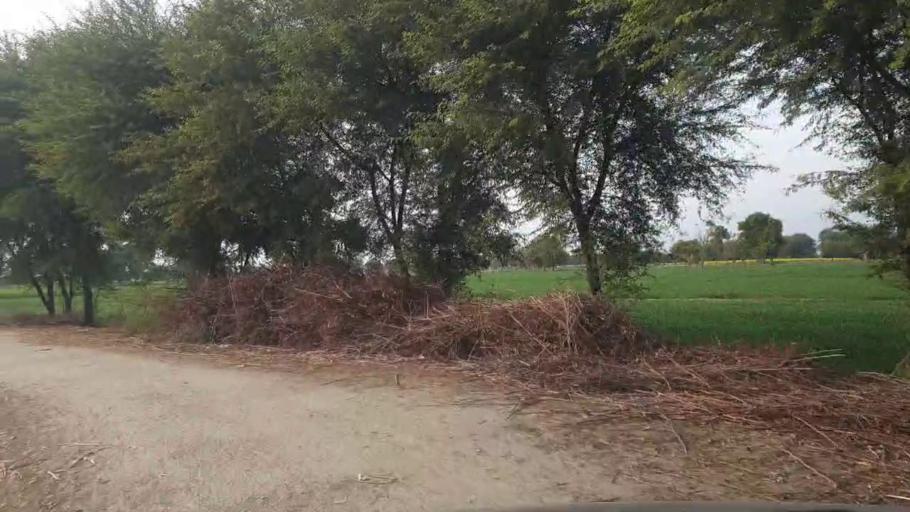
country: PK
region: Sindh
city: Shahpur Chakar
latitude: 26.1255
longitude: 68.5546
